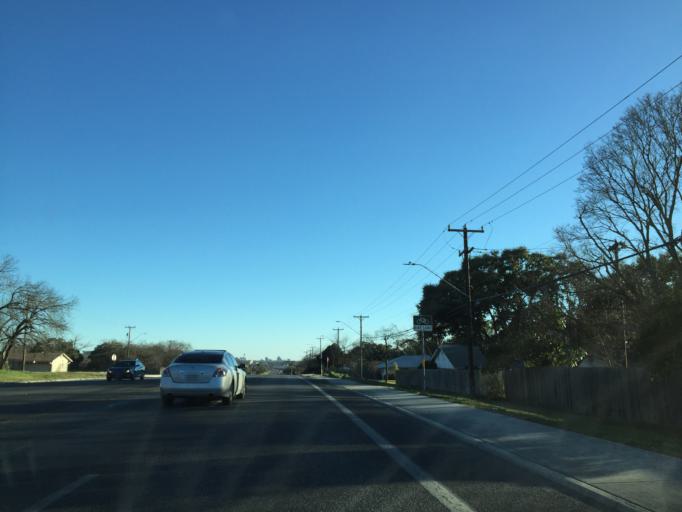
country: US
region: Texas
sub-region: Bexar County
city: Castle Hills
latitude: 29.5334
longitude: -98.5062
